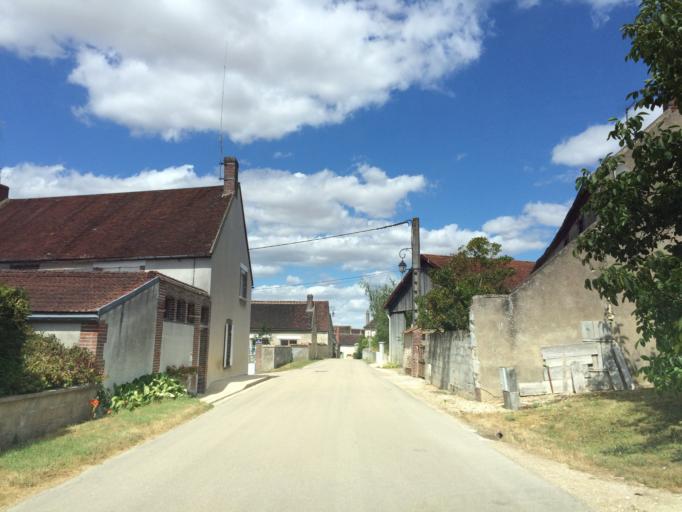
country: FR
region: Bourgogne
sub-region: Departement de l'Yonne
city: Fleury-la-Vallee
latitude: 47.9120
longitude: 3.4752
